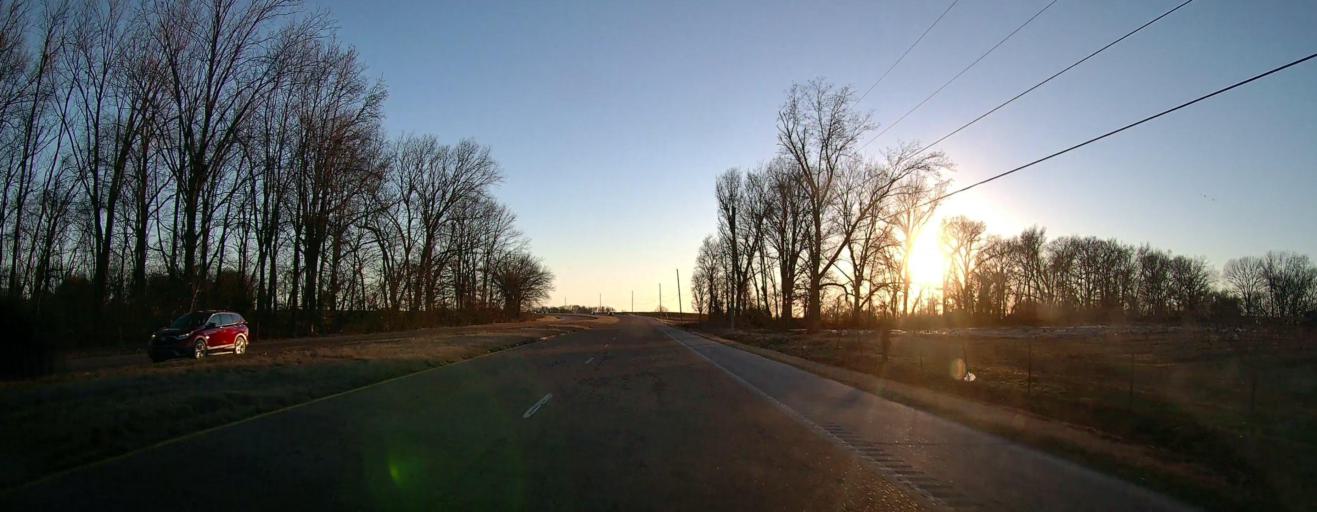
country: US
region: Tennessee
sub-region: Shelby County
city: Millington
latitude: 35.3130
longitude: -89.8782
